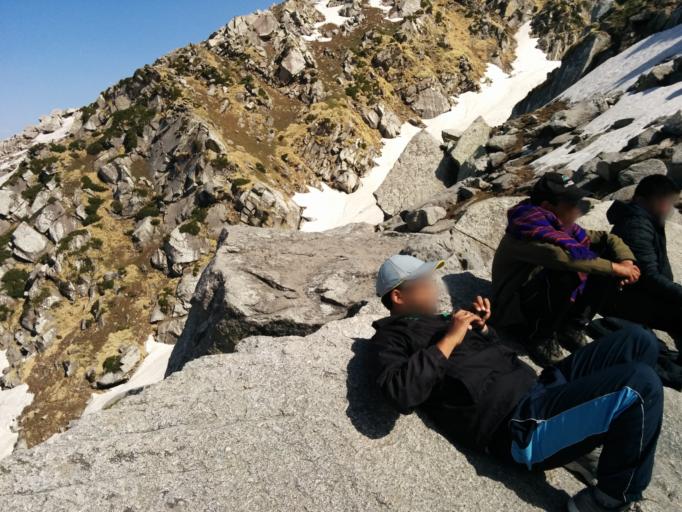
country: IN
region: Himachal Pradesh
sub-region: Kangra
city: Dharmsala
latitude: 32.2875
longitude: 76.3721
